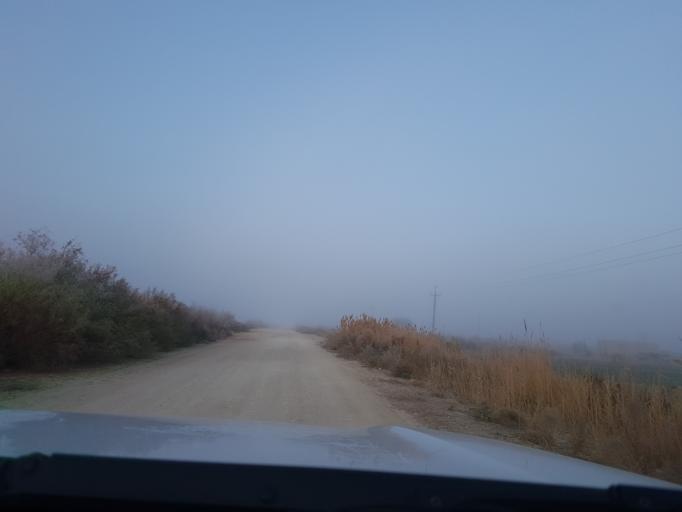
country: TM
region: Dasoguz
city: Koeneuergench
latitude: 41.8452
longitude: 58.4549
